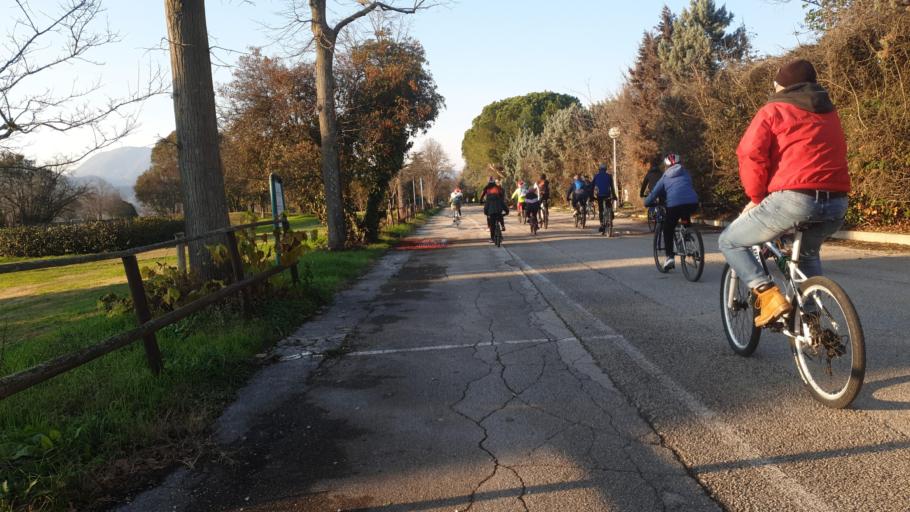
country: IT
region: Veneto
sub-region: Provincia di Padova
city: Battaglia Terme
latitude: 45.2887
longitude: 11.7681
